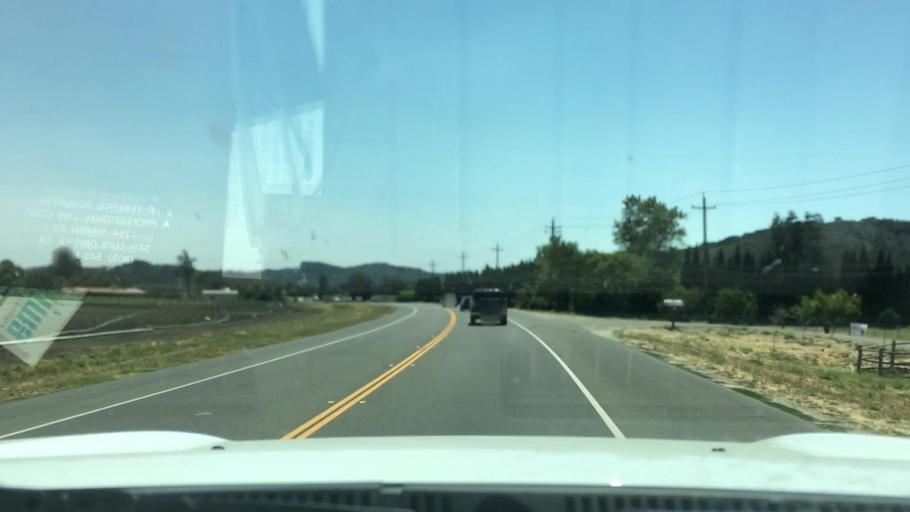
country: US
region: California
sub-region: San Luis Obispo County
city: Pismo Beach
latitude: 35.2106
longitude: -120.6160
